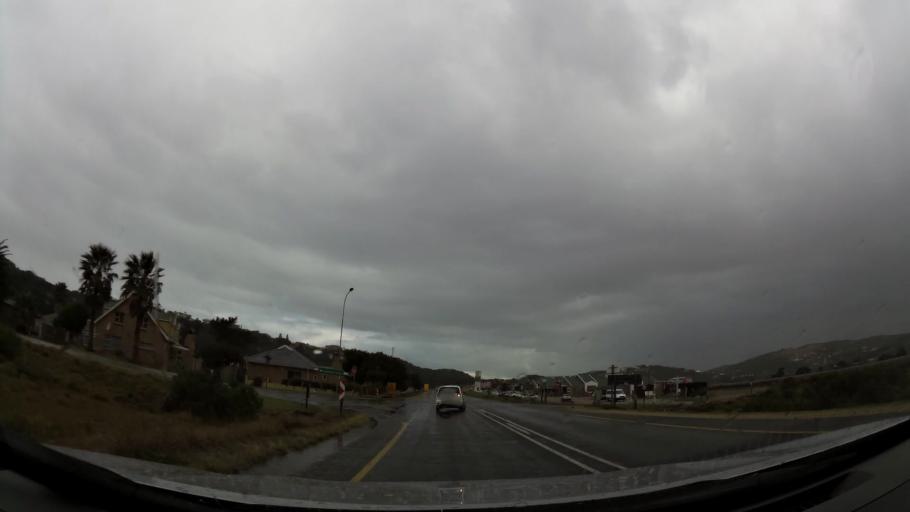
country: ZA
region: Western Cape
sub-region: Eden District Municipality
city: Mossel Bay
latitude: -34.0531
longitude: 22.2275
